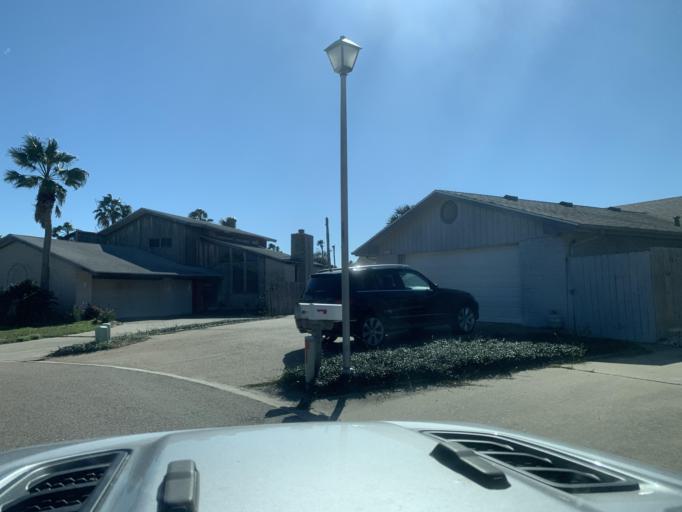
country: US
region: Texas
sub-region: Nueces County
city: Corpus Christi
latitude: 27.6250
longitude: -97.2282
